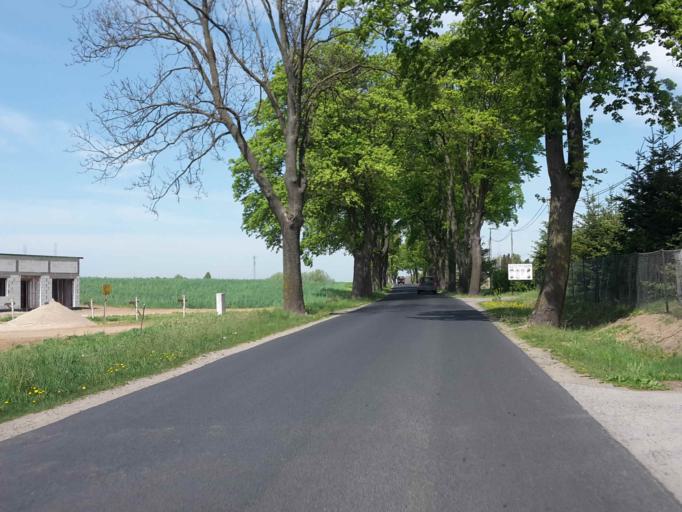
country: PL
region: Kujawsko-Pomorskie
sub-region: Powiat brodnicki
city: Brodnica
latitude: 53.3200
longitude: 19.3810
